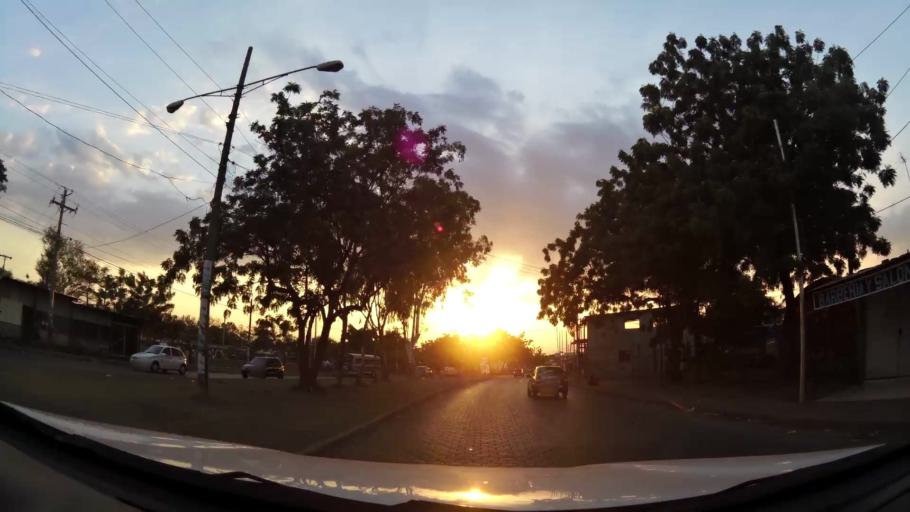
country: NI
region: Managua
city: Managua
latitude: 12.1339
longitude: -86.1972
